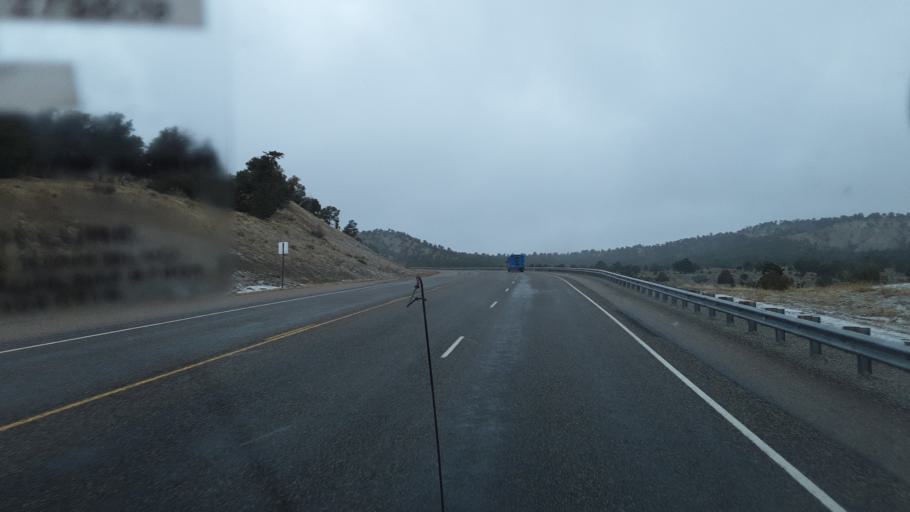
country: US
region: New Mexico
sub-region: Rio Arriba County
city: Tierra Amarilla
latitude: 36.4621
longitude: -106.4791
